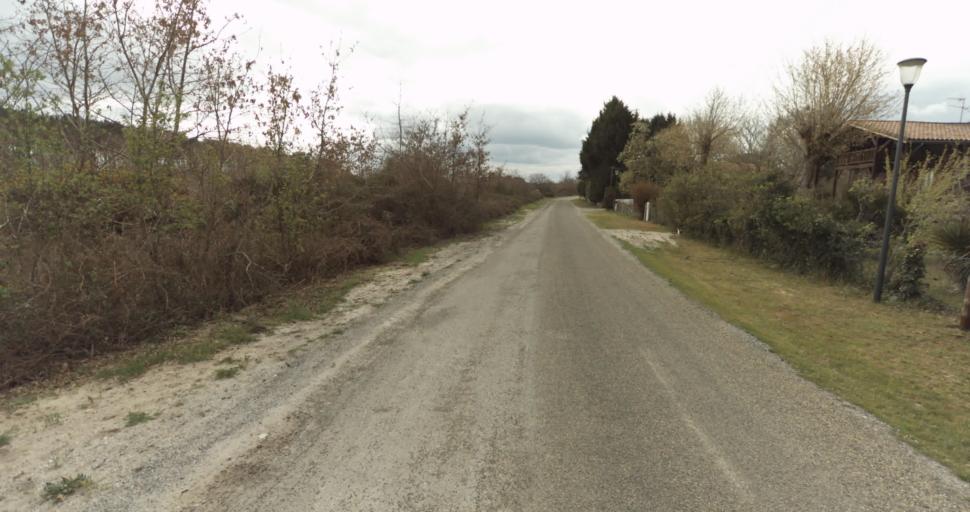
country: FR
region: Aquitaine
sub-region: Departement des Landes
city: Roquefort
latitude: 44.0468
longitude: -0.3229
